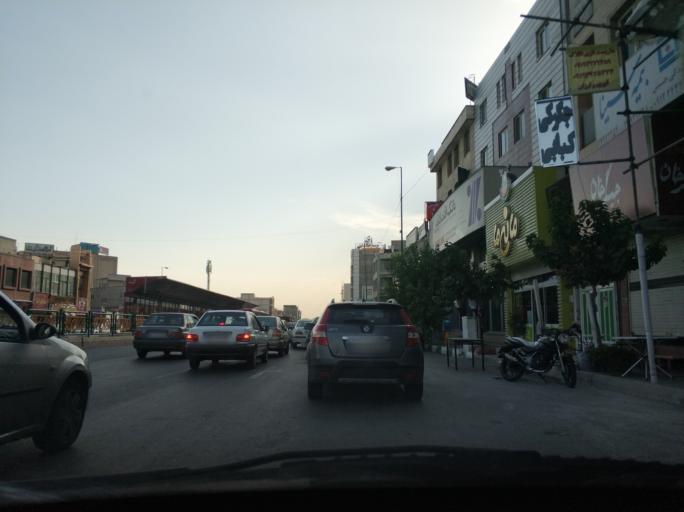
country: IR
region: Tehran
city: Tehran
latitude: 35.7152
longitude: 51.4918
